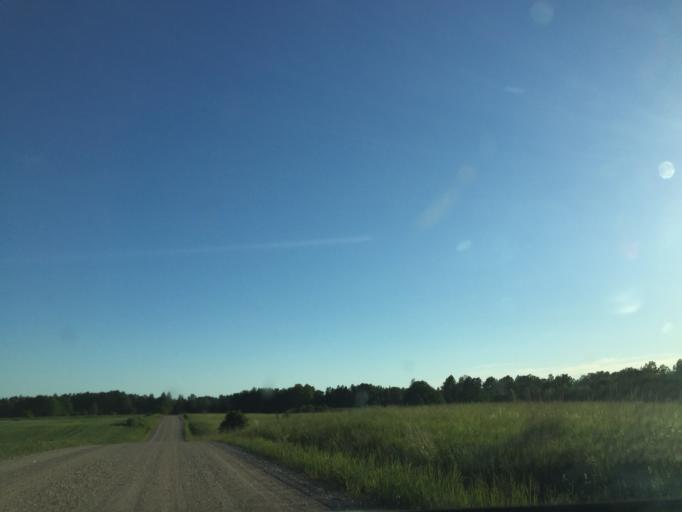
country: LV
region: Broceni
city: Broceni
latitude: 56.8296
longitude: 22.5604
